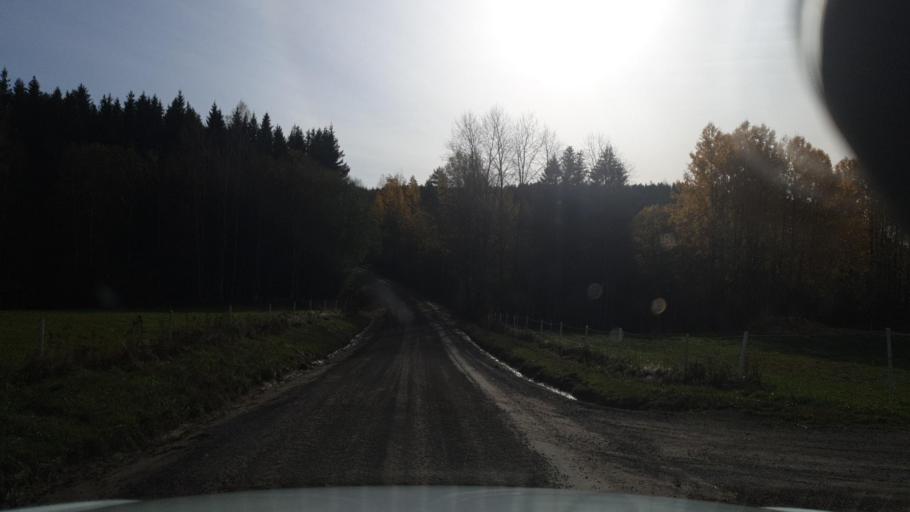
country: NO
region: Hedmark
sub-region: Eidskog
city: Skotterud
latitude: 59.7321
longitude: 12.0971
